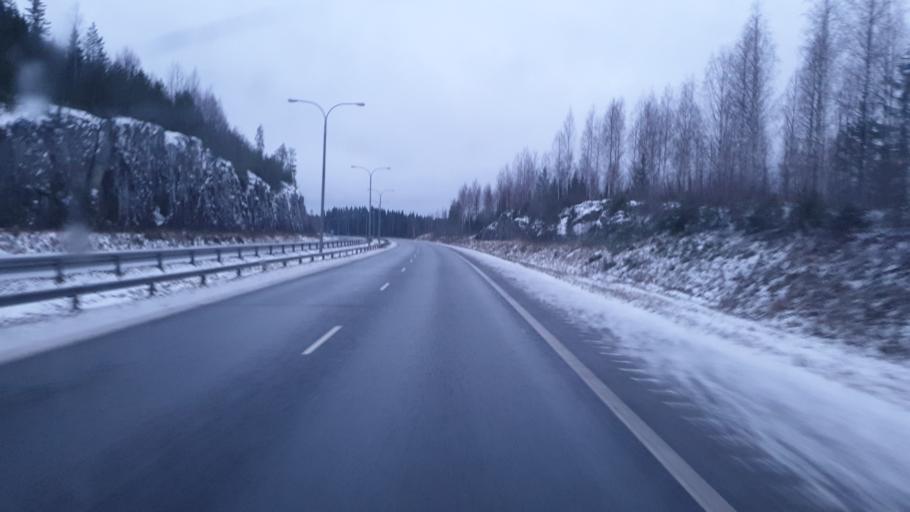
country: FI
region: Northern Savo
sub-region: Kuopio
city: Siilinjaervi
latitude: 63.0377
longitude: 27.6589
